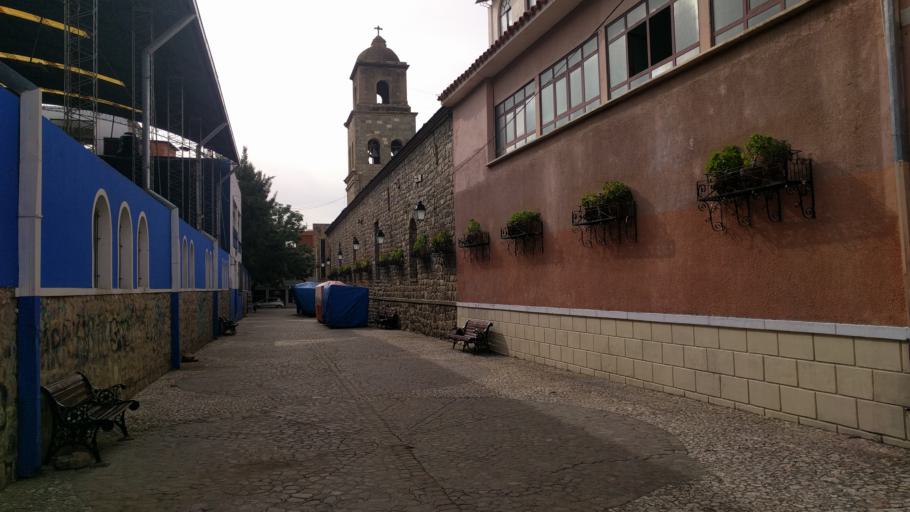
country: BO
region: Tarija
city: Tarija
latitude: -21.5328
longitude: -64.7361
